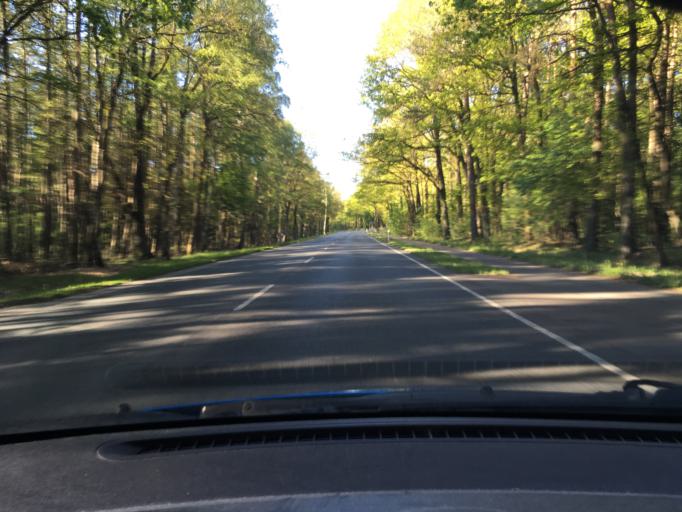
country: DE
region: Lower Saxony
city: Soltau
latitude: 53.0472
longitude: 9.8573
